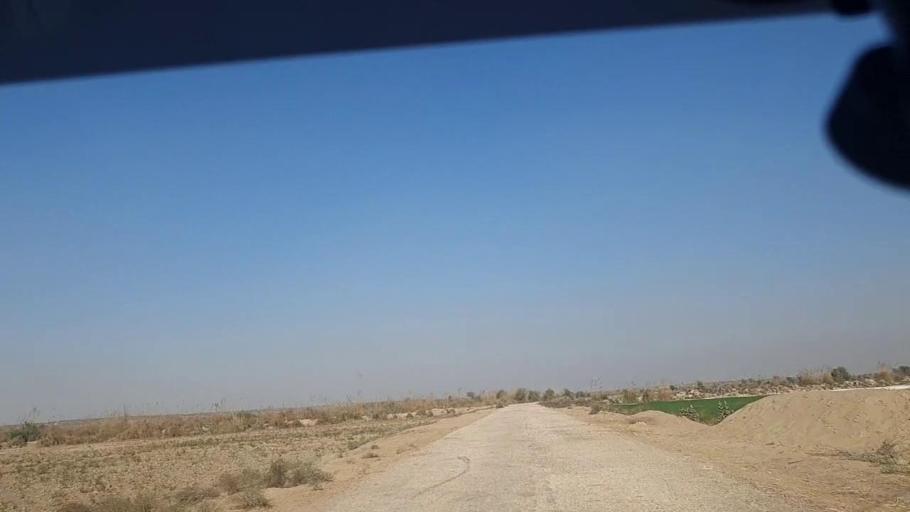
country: PK
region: Sindh
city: Khanpur
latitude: 27.5649
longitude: 69.3385
